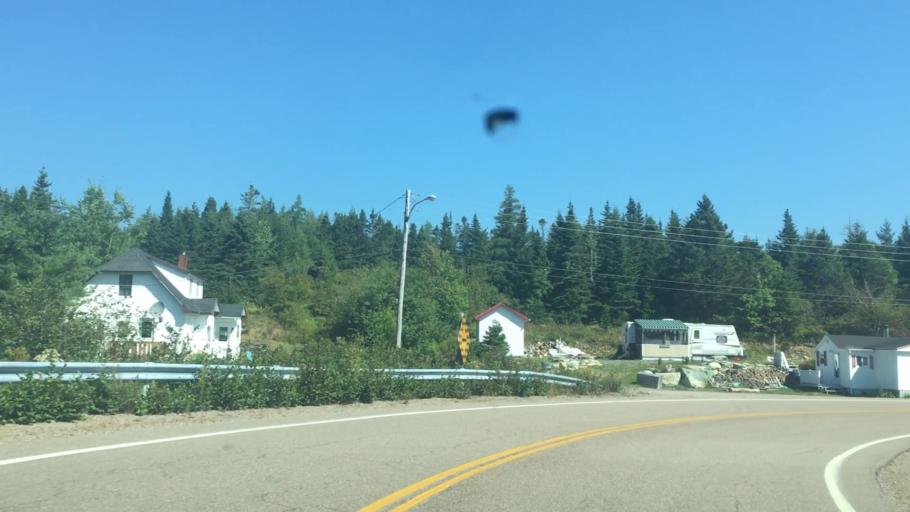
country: CA
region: Nova Scotia
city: Antigonish
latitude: 45.0280
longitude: -62.0309
